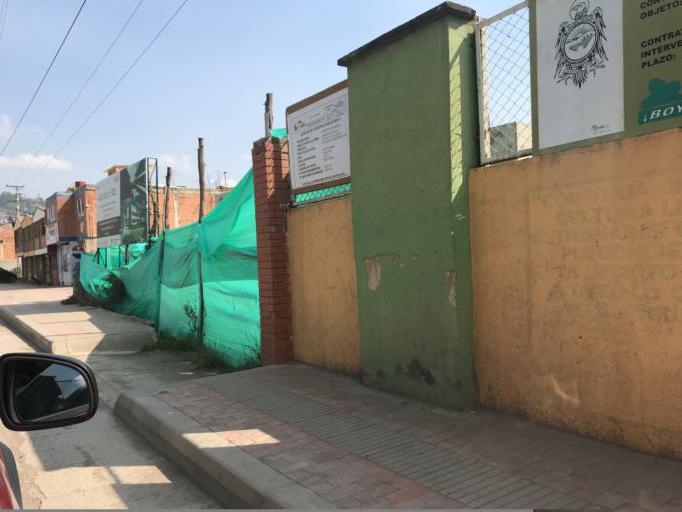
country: CO
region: Boyaca
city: Samaca
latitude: 5.4967
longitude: -73.4886
